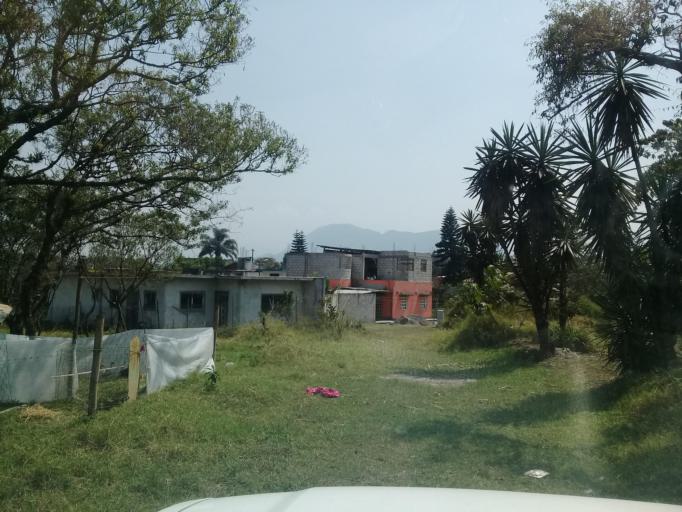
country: MX
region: Veracruz
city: Ixtac Zoquitlan
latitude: 18.8737
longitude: -97.0589
